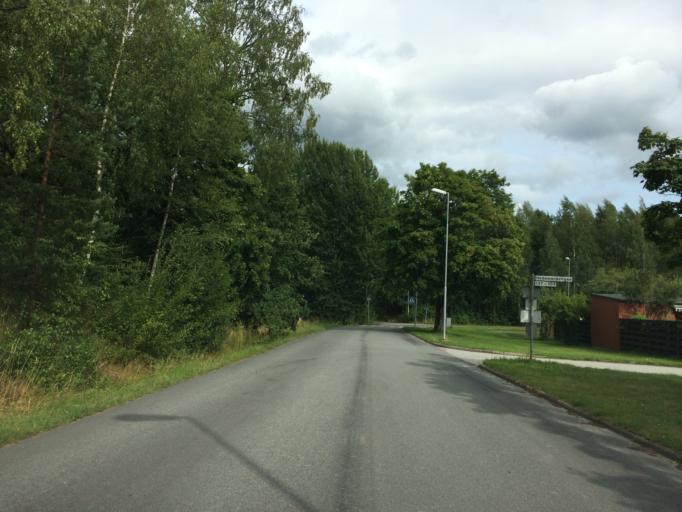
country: SE
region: Stockholm
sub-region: Upplands Vasby Kommun
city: Upplands Vaesby
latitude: 59.4656
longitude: 17.9078
